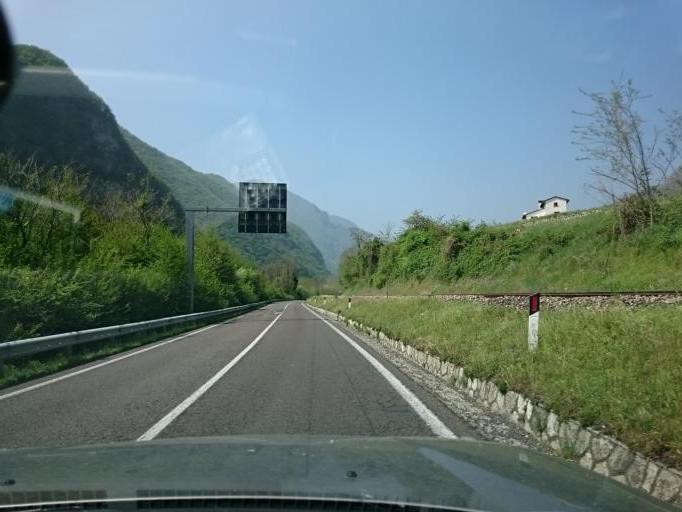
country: IT
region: Veneto
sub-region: Provincia di Vicenza
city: Campolongo sul Brenta
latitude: 45.8322
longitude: 11.7000
